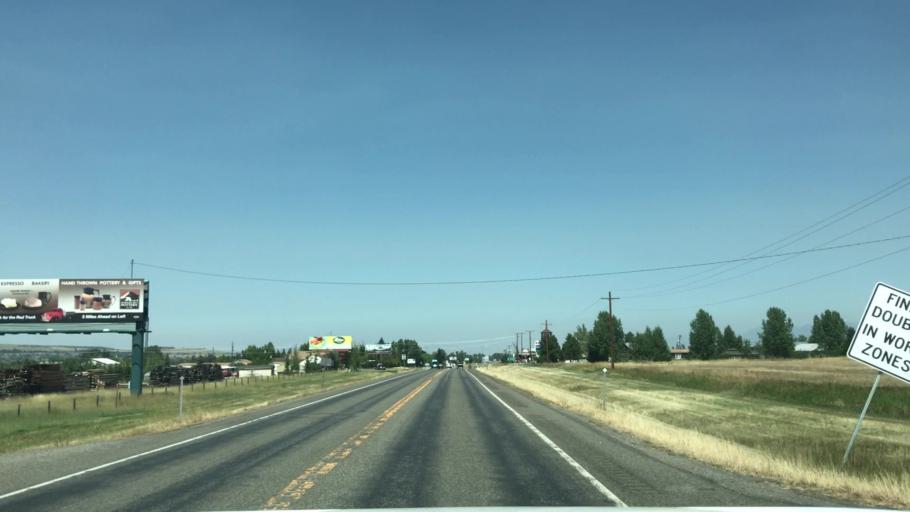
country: US
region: Montana
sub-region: Gallatin County
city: Four Corners
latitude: 45.5875
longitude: -111.1971
